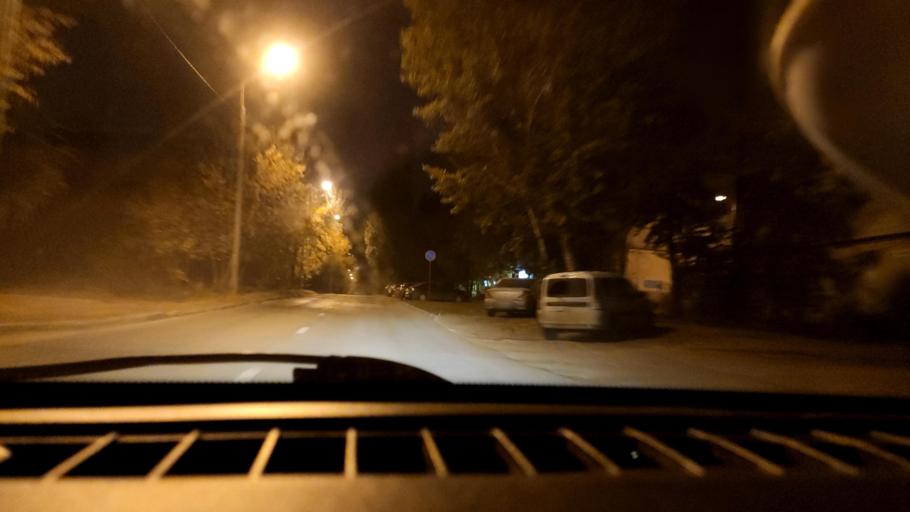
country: RU
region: Samara
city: Samara
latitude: 53.2348
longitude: 50.2321
